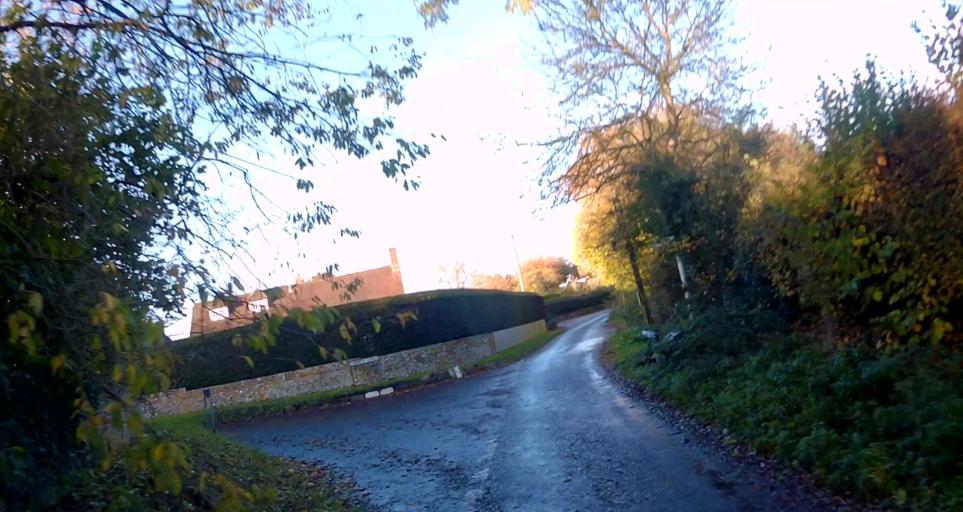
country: GB
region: England
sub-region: Hampshire
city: Basingstoke
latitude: 51.2066
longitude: -1.0795
